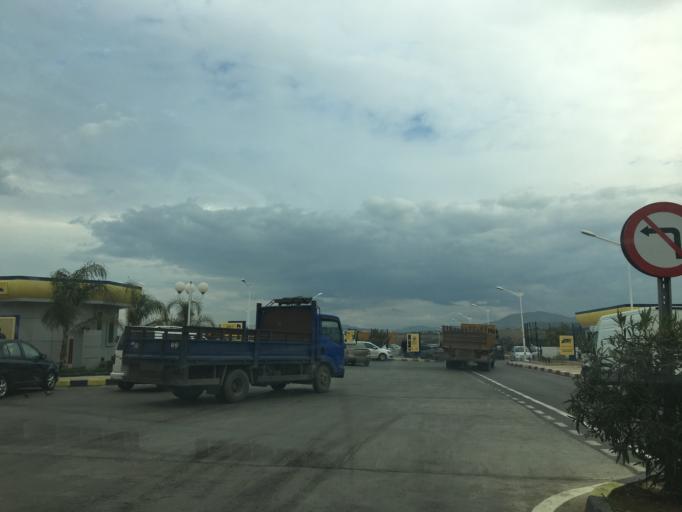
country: DZ
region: Bouira
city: Bouira
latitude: 36.3100
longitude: 4.0608
